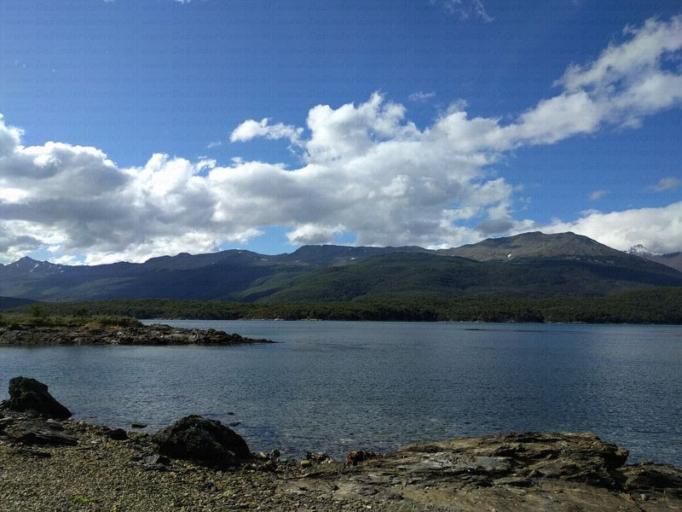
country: AR
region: Tierra del Fuego
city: Ushuaia
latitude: -54.8608
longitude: -68.5604
